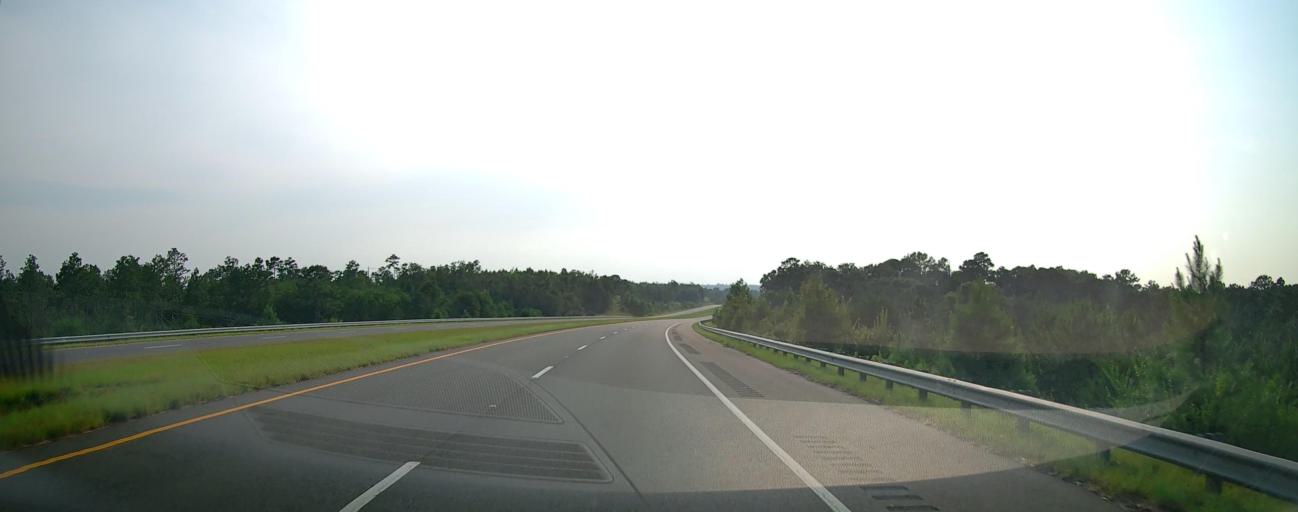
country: US
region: Georgia
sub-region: Talbot County
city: Talbotton
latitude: 32.5969
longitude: -84.4556
